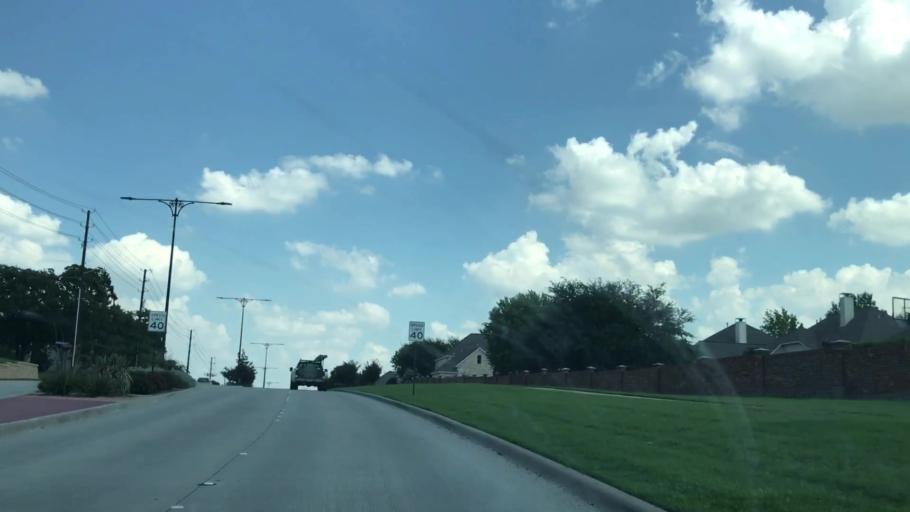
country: US
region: Texas
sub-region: Dallas County
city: Coppell
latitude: 32.9696
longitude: -97.0060
